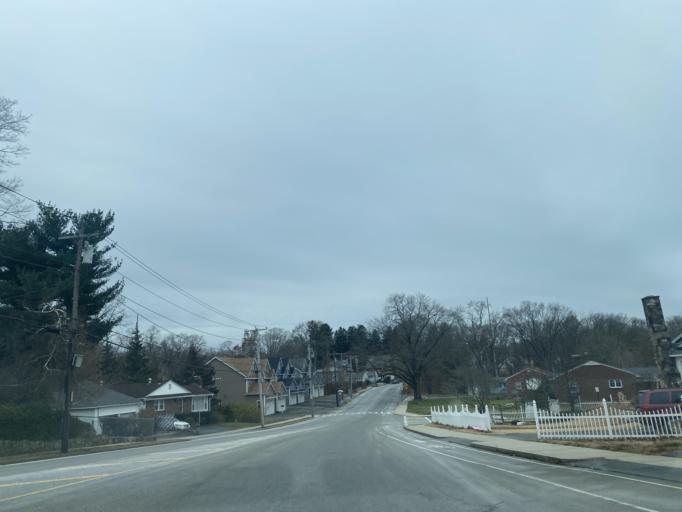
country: US
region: Massachusetts
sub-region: Worcester County
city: Hamilton
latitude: 42.2597
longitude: -71.7592
